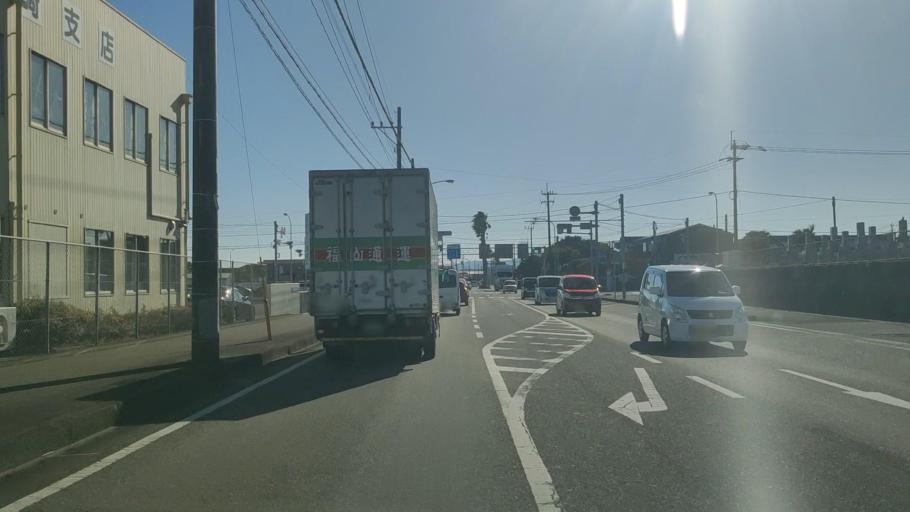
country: JP
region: Miyazaki
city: Miyazaki-shi
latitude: 31.9402
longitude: 131.4570
